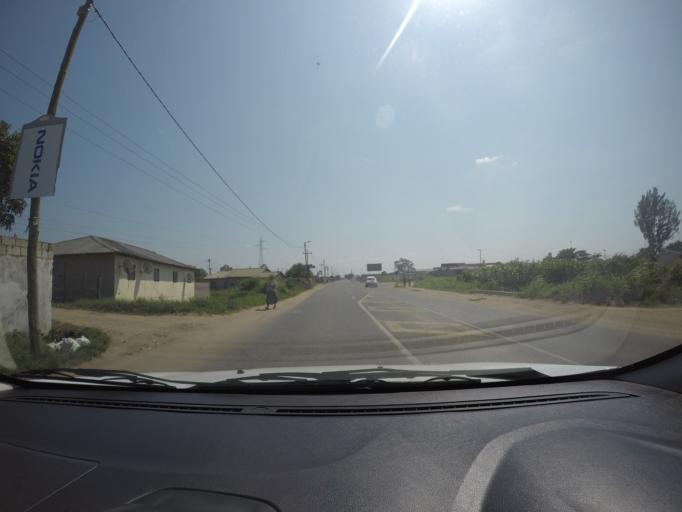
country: ZA
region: KwaZulu-Natal
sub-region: uThungulu District Municipality
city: eSikhawini
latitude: -28.8684
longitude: 31.9053
